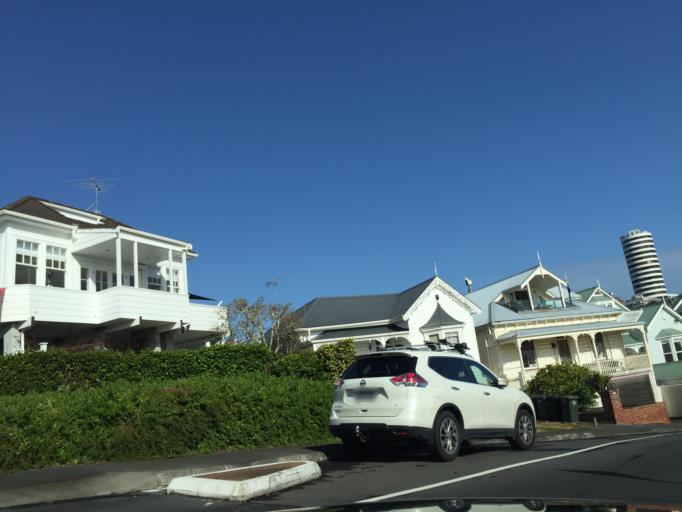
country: NZ
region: Auckland
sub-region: Auckland
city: Auckland
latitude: -36.8437
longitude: 174.7459
